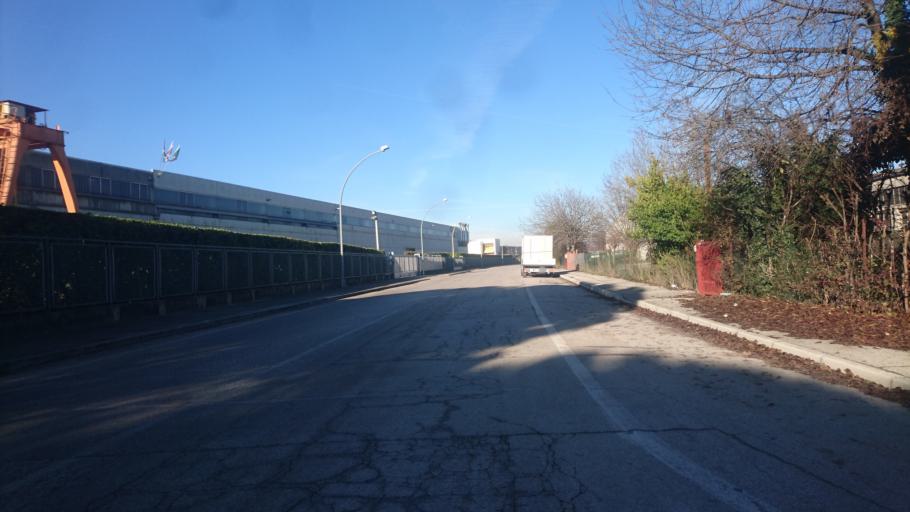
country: IT
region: Veneto
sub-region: Provincia di Padova
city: Limena
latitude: 45.4578
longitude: 11.8493
